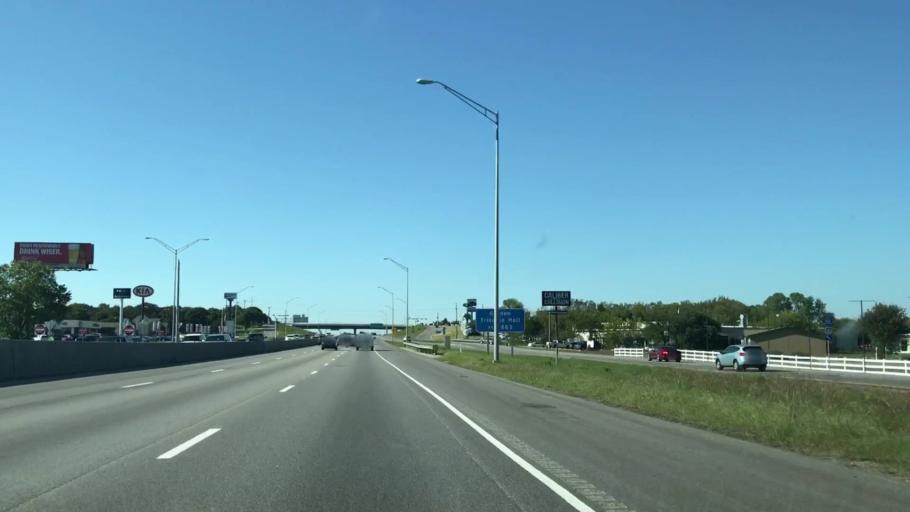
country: US
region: Texas
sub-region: Denton County
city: Corinth
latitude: 33.1588
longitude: -97.0681
